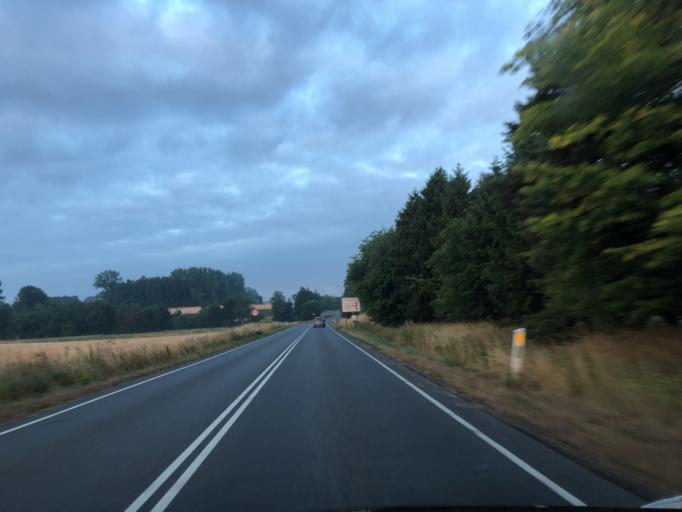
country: DK
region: Zealand
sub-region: Soro Kommune
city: Dianalund
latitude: 55.4928
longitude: 11.5130
